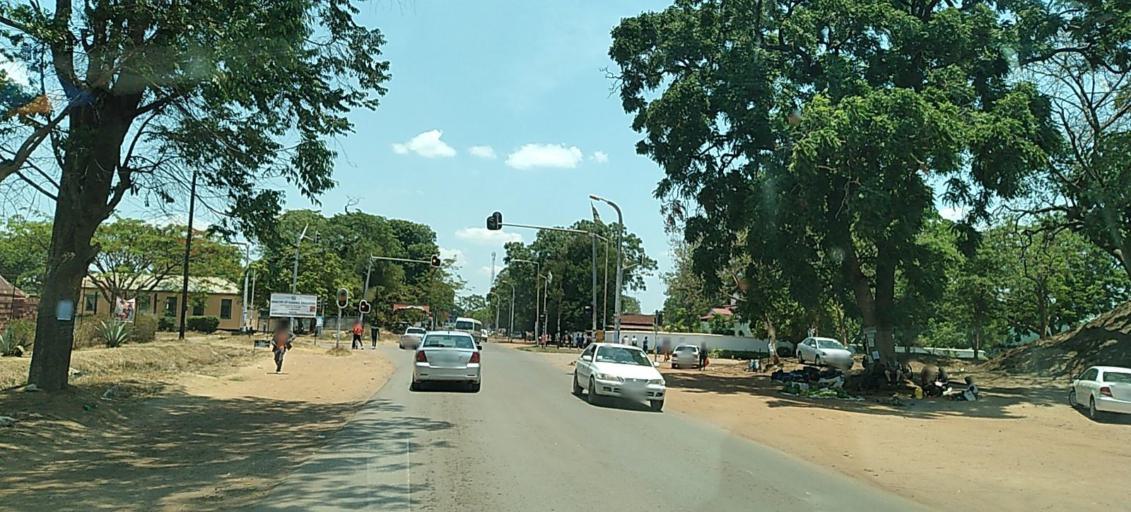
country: ZM
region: Copperbelt
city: Luanshya
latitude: -13.1357
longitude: 28.4201
